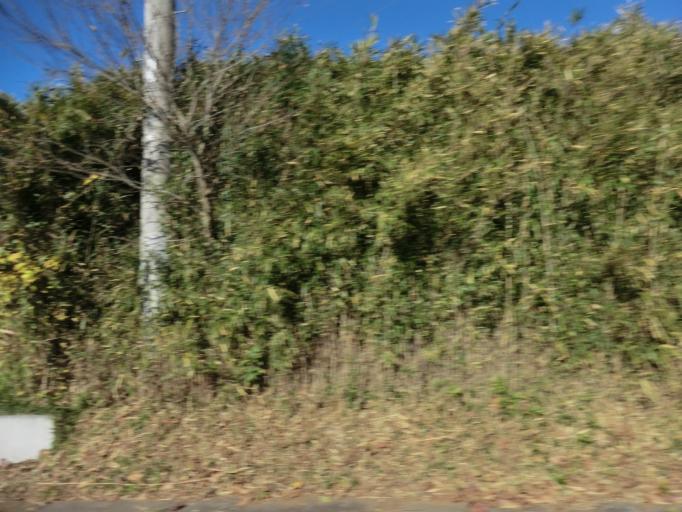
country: JP
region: Ibaraki
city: Ishioka
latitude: 36.1594
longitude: 140.3272
